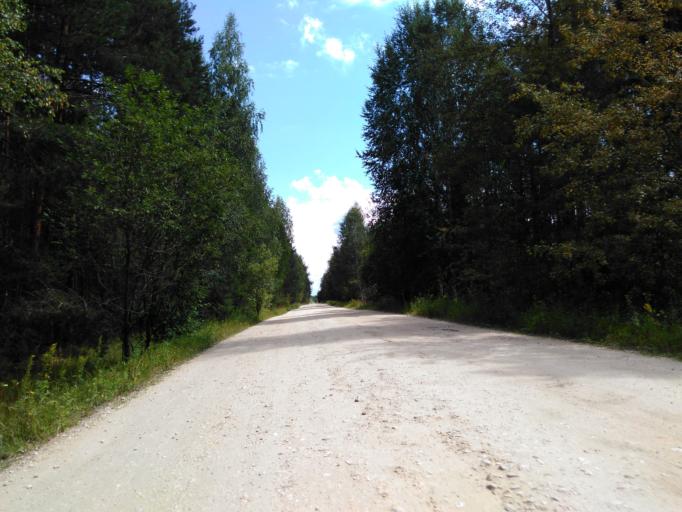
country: RU
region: Vladimir
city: Krasnyy Oktyabr'
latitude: 56.0046
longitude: 38.8380
